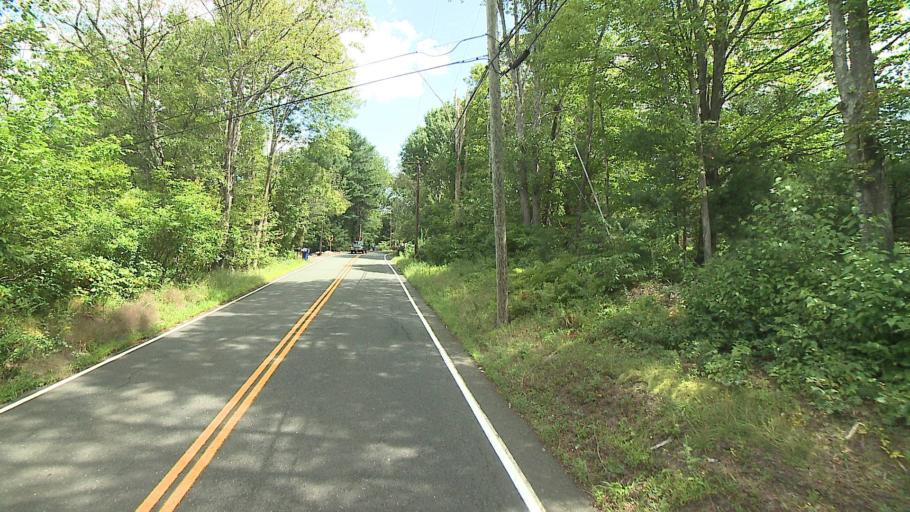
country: US
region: Connecticut
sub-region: Tolland County
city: Crystal Lake
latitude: 41.9355
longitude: -72.3467
